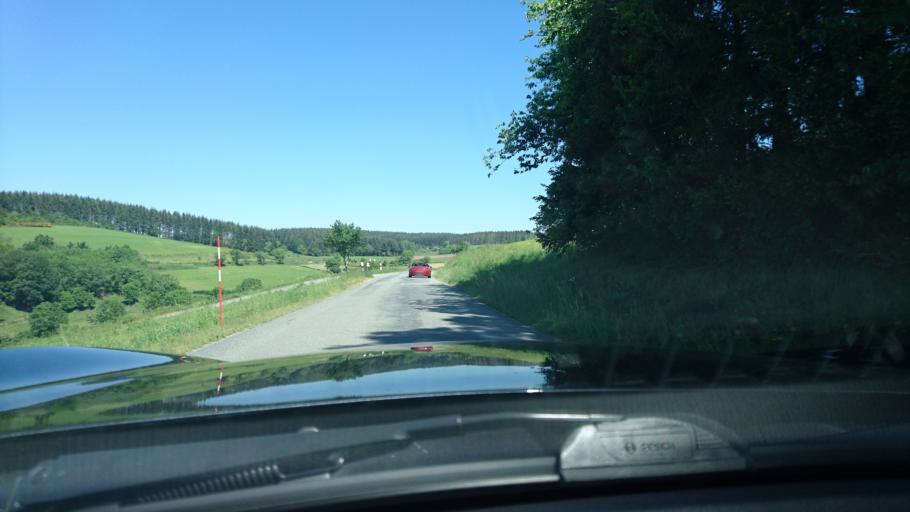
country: FR
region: Rhone-Alpes
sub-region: Departement de la Loire
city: Violay
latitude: 45.8911
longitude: 4.3291
